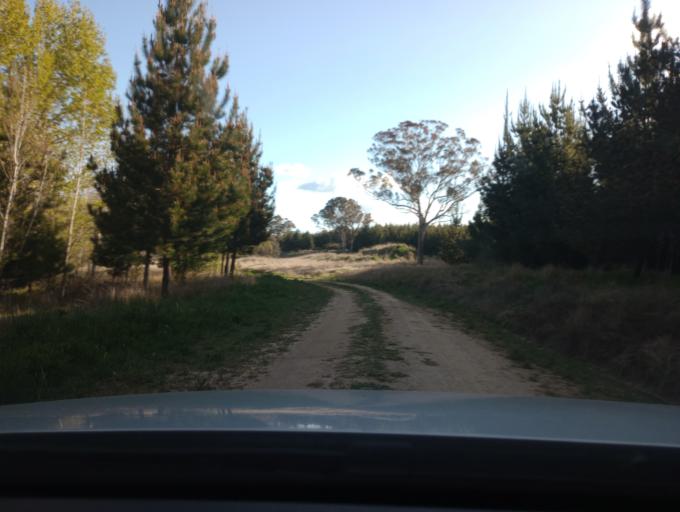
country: AU
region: New South Wales
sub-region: Blayney
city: Millthorpe
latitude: -33.4054
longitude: 149.3112
